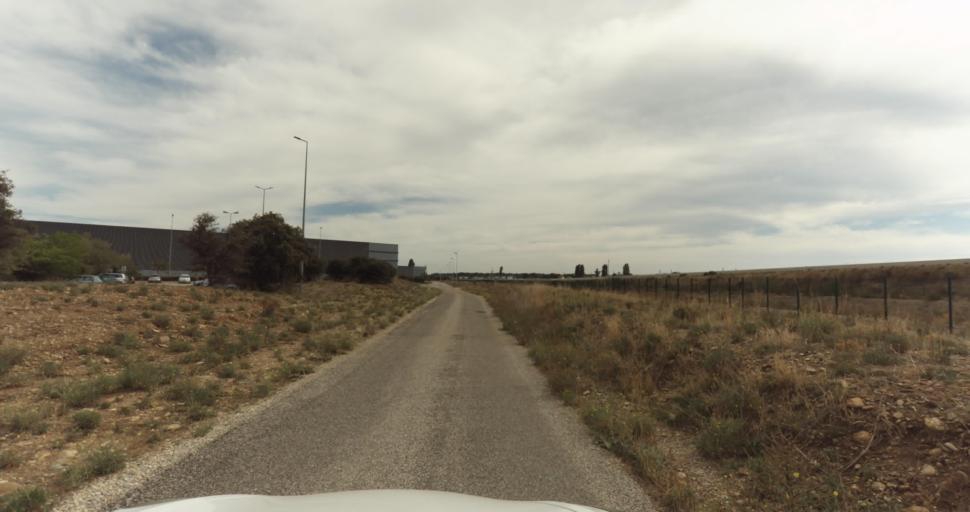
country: FR
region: Provence-Alpes-Cote d'Azur
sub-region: Departement des Bouches-du-Rhone
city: Miramas
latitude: 43.6000
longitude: 4.9918
